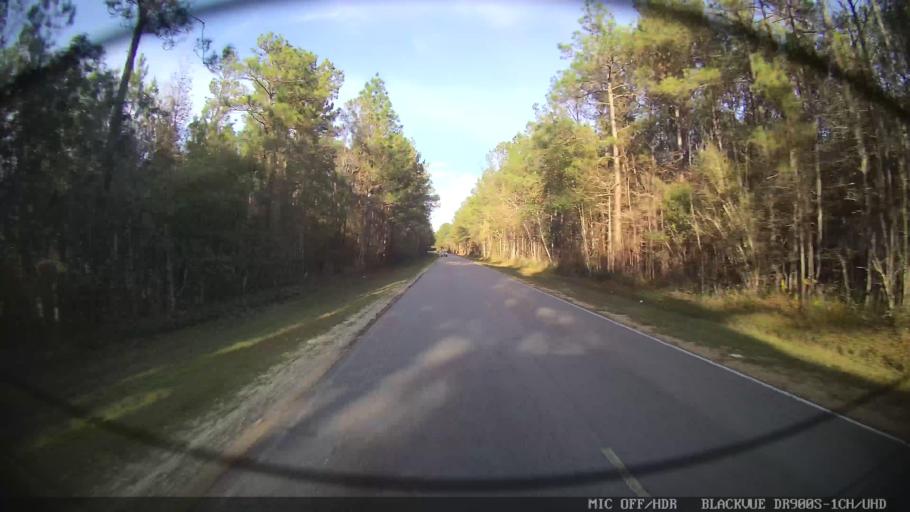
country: US
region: Mississippi
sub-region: Lamar County
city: Purvis
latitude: 31.1617
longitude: -89.3293
